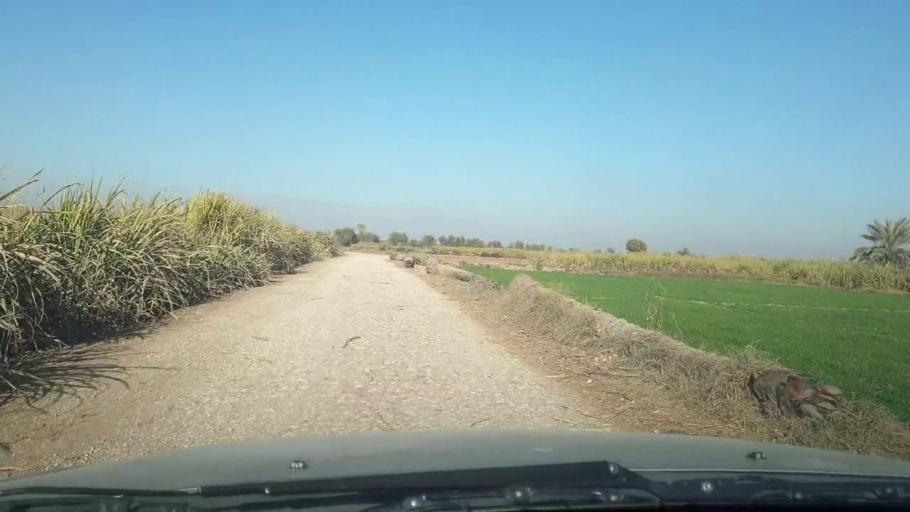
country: PK
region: Sindh
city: Adilpur
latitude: 27.9520
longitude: 69.1978
